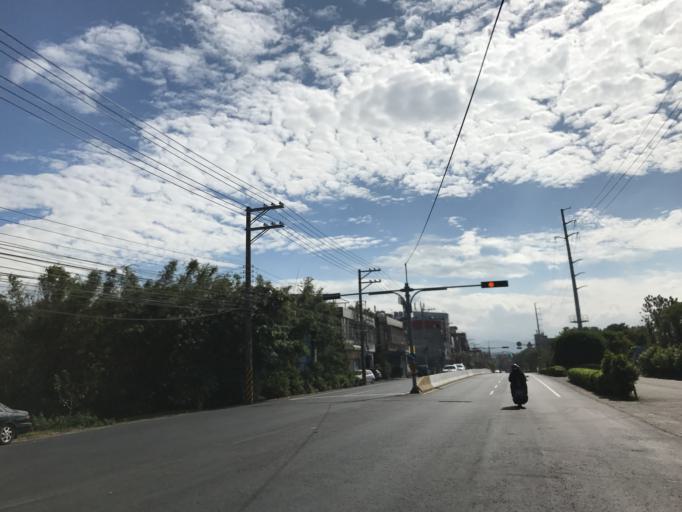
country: TW
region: Taiwan
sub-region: Hsinchu
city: Zhubei
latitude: 24.7759
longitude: 121.0468
